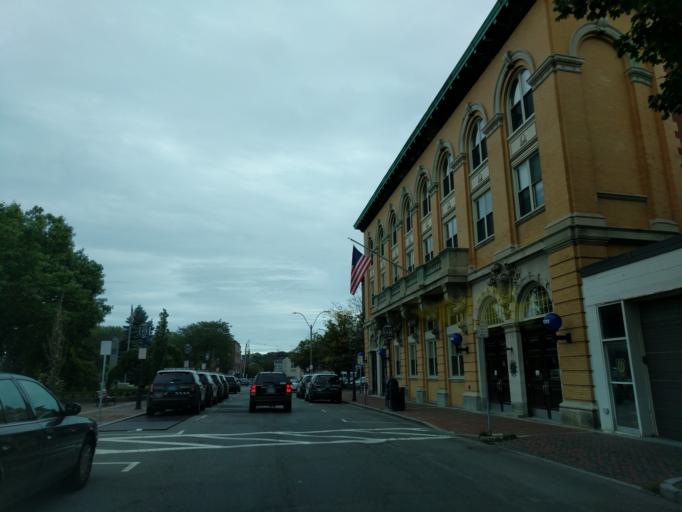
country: US
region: Massachusetts
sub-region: Suffolk County
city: Chelsea
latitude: 42.3891
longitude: -71.0405
